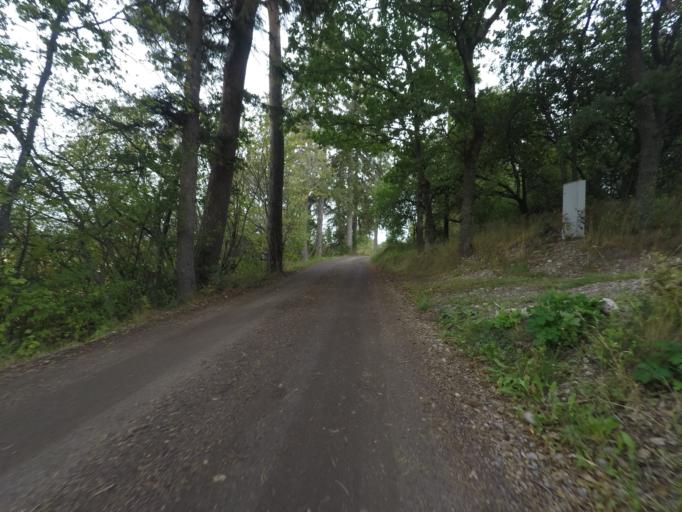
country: SE
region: Vaestmanland
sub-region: Kungsors Kommun
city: Kungsoer
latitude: 59.4601
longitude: 16.0715
